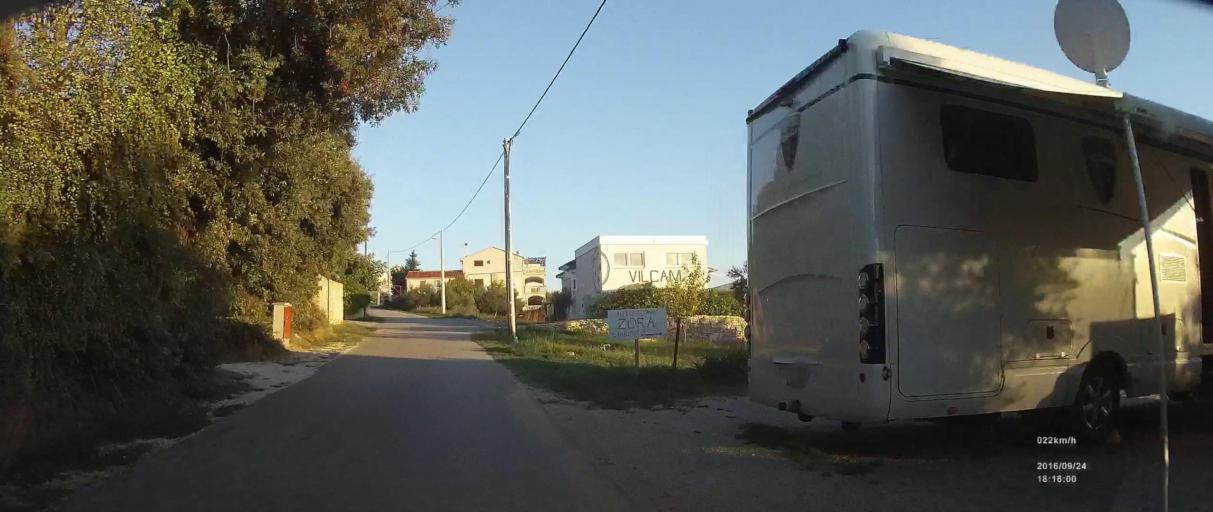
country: HR
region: Zadarska
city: Pakostane
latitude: 43.9052
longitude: 15.5172
